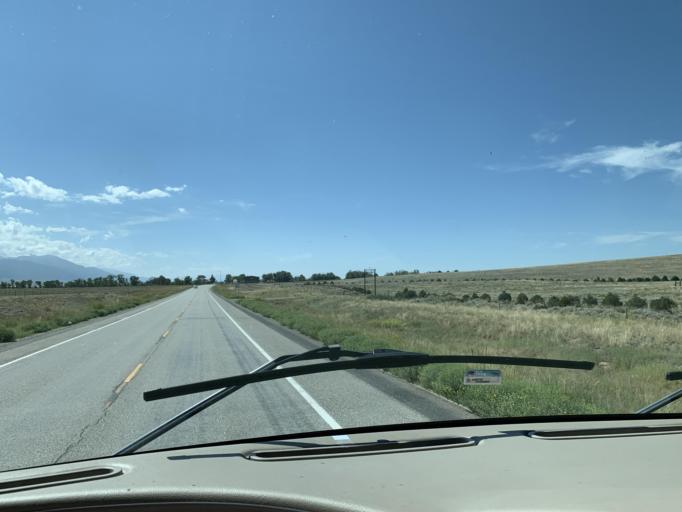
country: US
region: Colorado
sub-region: Saguache County
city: Saguache
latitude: 38.2556
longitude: -105.9542
